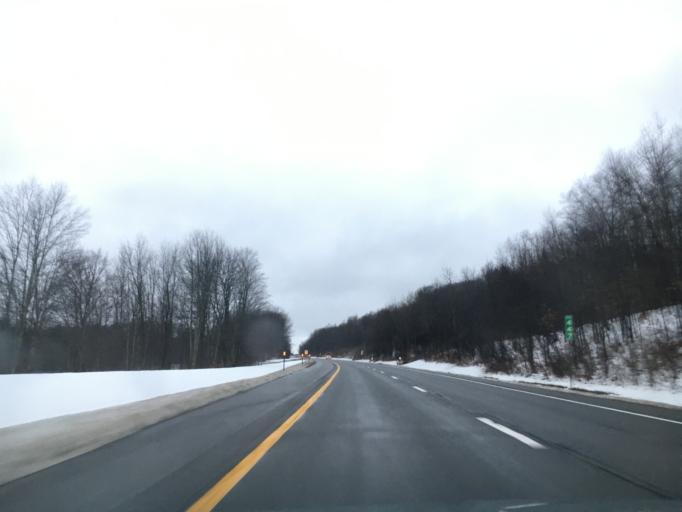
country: US
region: New York
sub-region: Cortland County
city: McGraw
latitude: 42.5203
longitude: -76.0808
